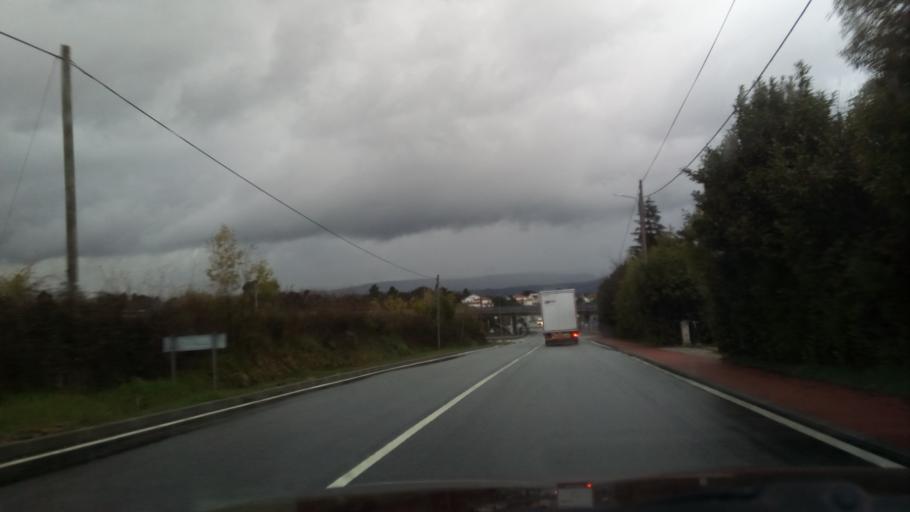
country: PT
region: Guarda
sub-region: Celorico da Beira
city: Celorico da Beira
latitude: 40.6349
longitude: -7.3491
